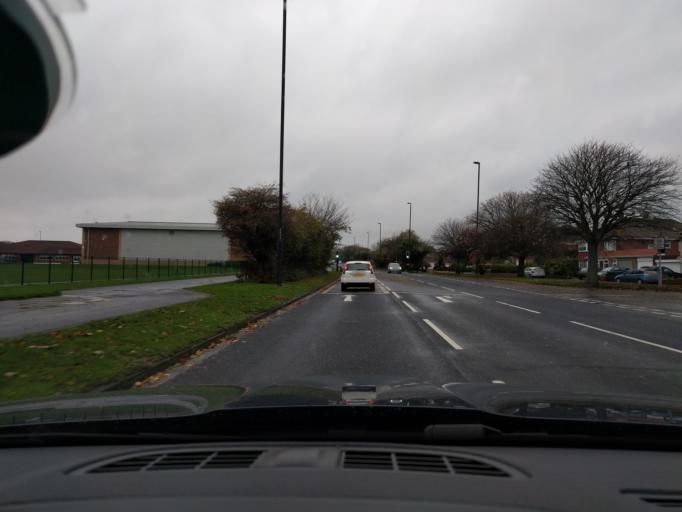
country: GB
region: England
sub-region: Borough of North Tyneside
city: North Shields
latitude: 55.0237
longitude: -1.4479
